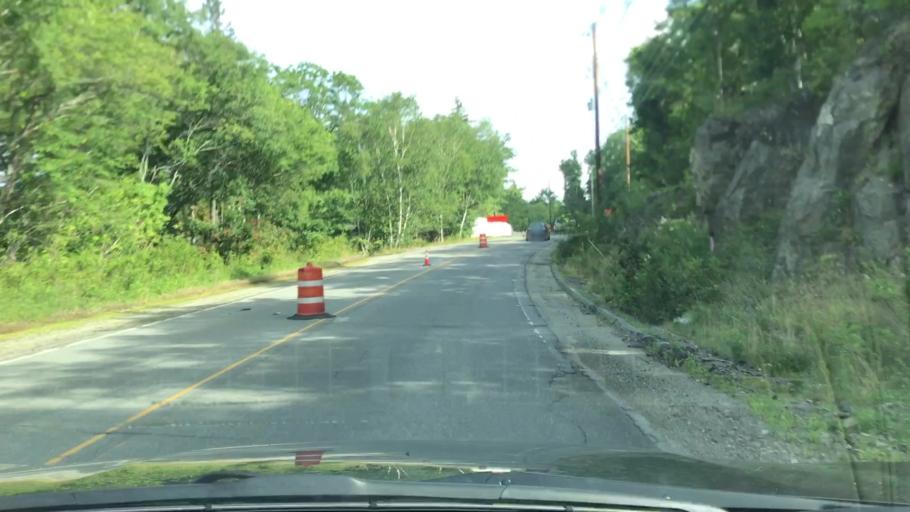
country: US
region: Maine
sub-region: Hancock County
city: Bar Harbor
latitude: 44.4055
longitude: -68.2352
